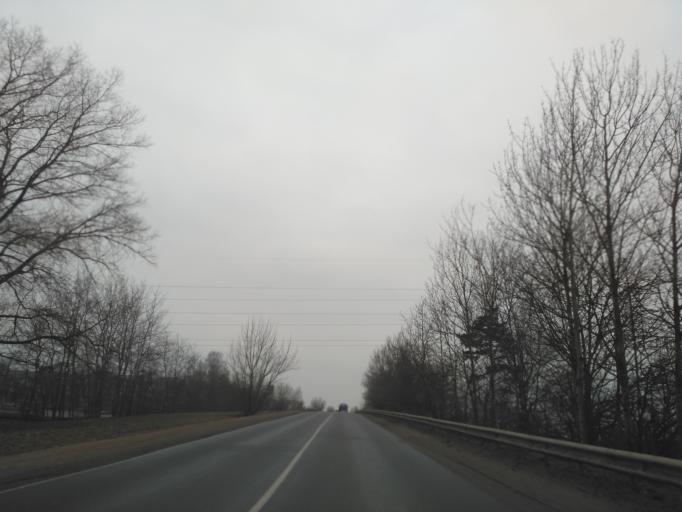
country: BY
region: Brest
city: Baranovichi
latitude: 53.1608
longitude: 26.0112
